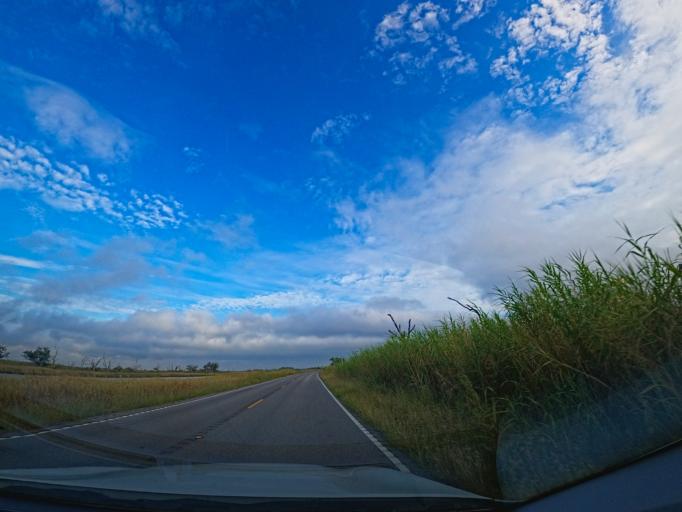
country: US
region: Louisiana
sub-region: Terrebonne Parish
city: Dulac
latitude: 29.3341
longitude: -90.6908
